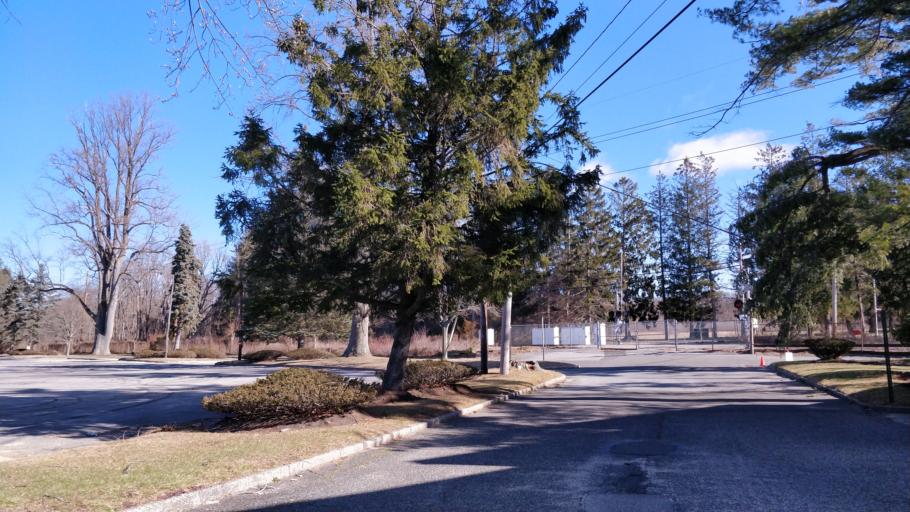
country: US
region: New York
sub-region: Suffolk County
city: Head of the Harbor
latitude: 40.8972
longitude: -73.1435
